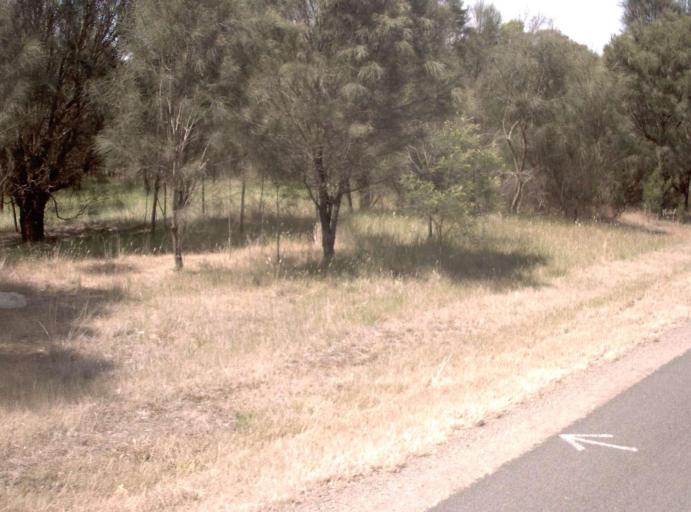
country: AU
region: Victoria
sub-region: Wellington
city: Sale
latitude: -38.1001
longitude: 146.9662
